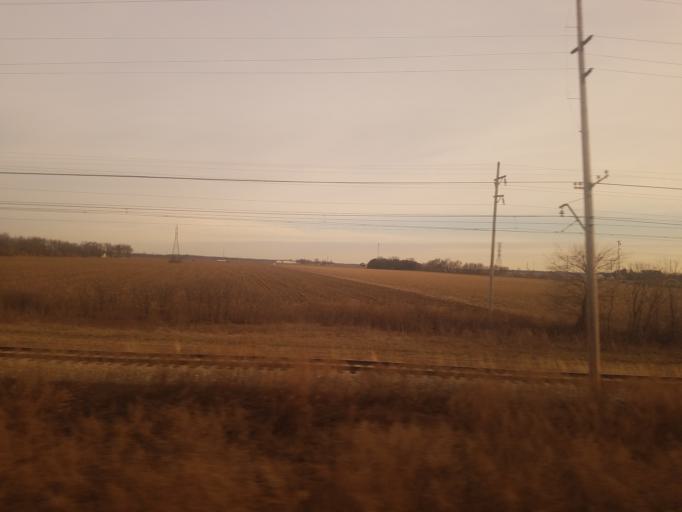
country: US
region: Indiana
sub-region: Saint Joseph County
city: New Carlisle
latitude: 41.7011
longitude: -86.4553
